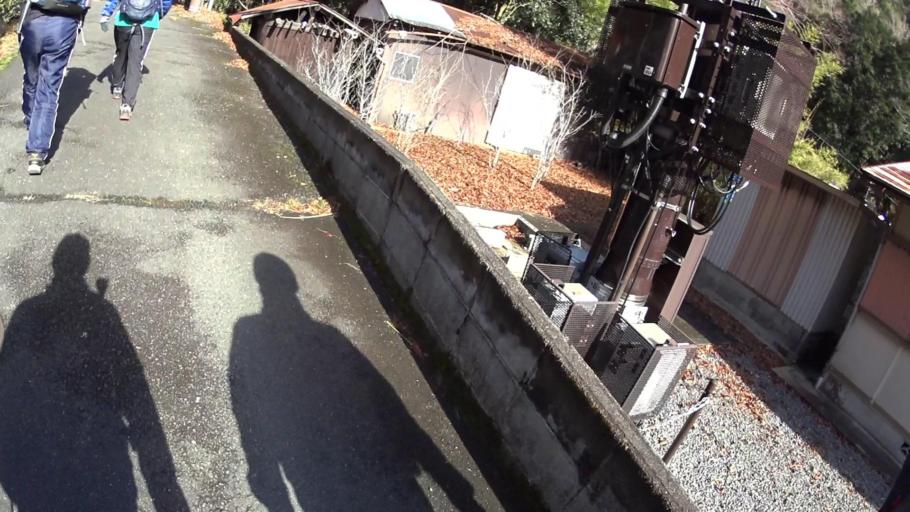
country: JP
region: Kyoto
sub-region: Kyoto-shi
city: Kamigyo-ku
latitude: 35.1000
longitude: 135.7609
